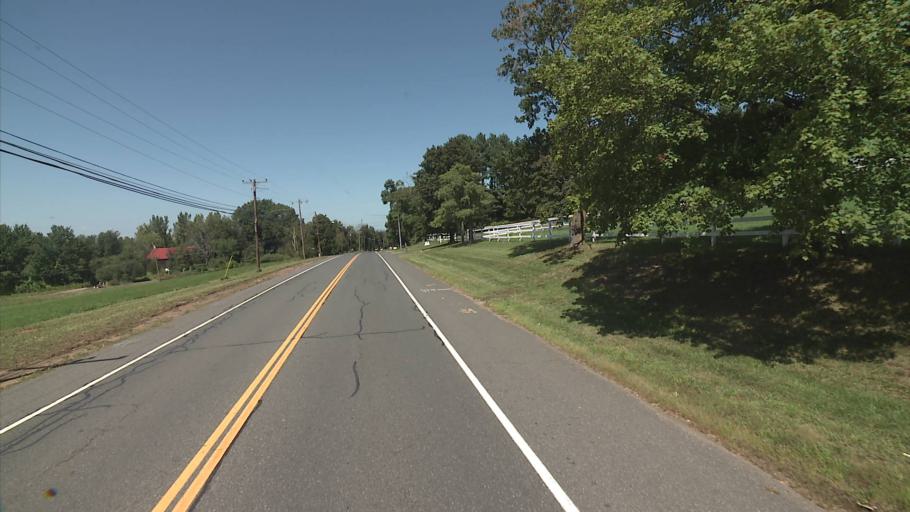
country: US
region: Connecticut
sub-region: Hartford County
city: Thompsonville
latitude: 42.0230
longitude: -72.6168
